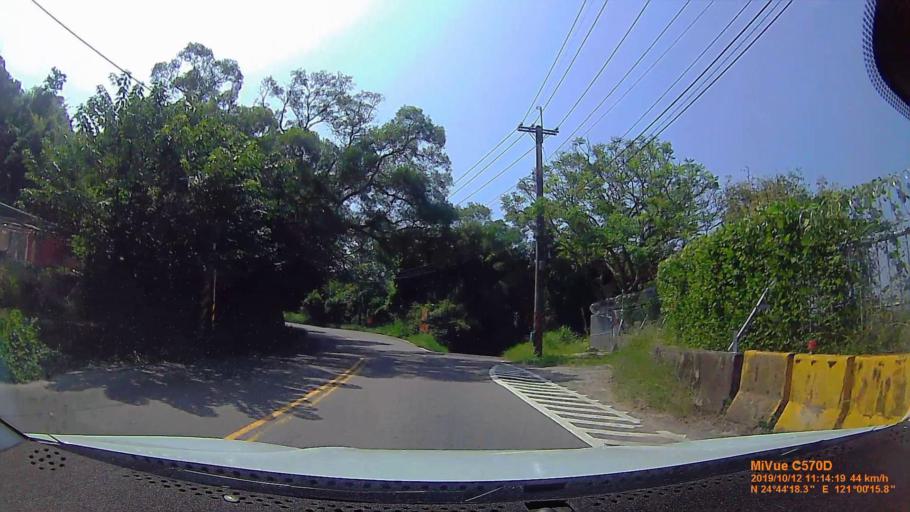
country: TW
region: Taiwan
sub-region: Hsinchu
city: Hsinchu
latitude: 24.7383
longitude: 121.0043
